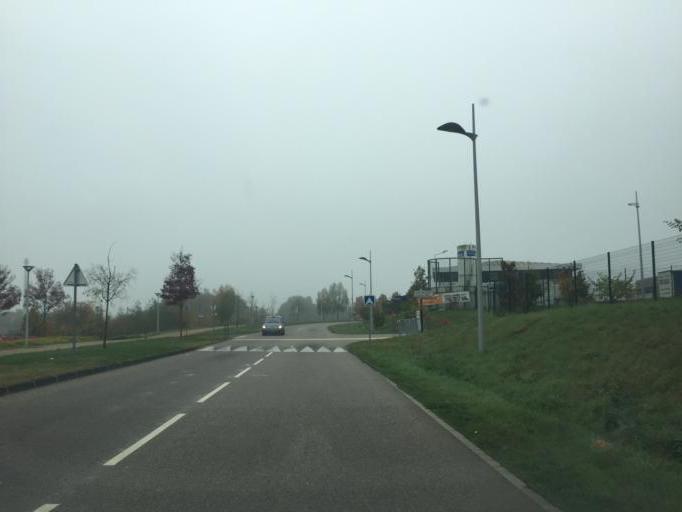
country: FR
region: Rhone-Alpes
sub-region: Departement du Rhone
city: Rillieux-la-Pape
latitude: 45.8218
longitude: 4.9156
